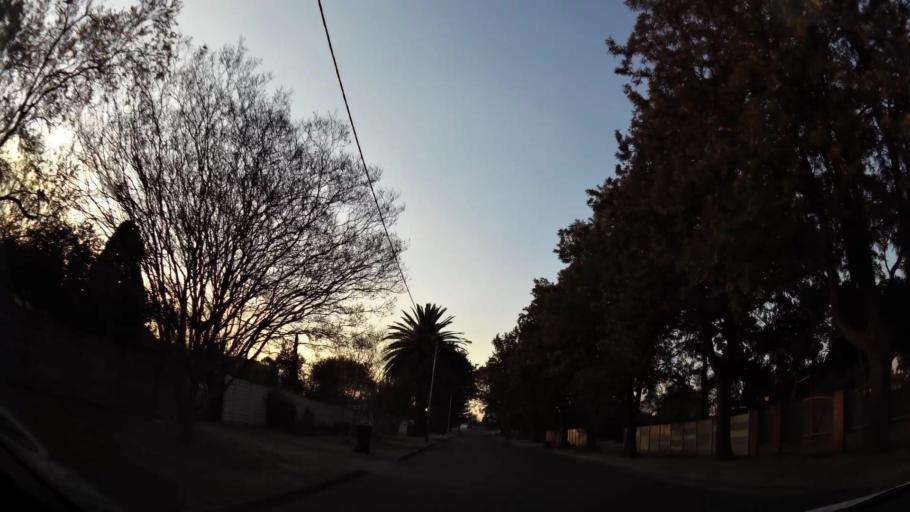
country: ZA
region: Gauteng
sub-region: Ekurhuleni Metropolitan Municipality
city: Springs
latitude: -26.3143
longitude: 28.4494
